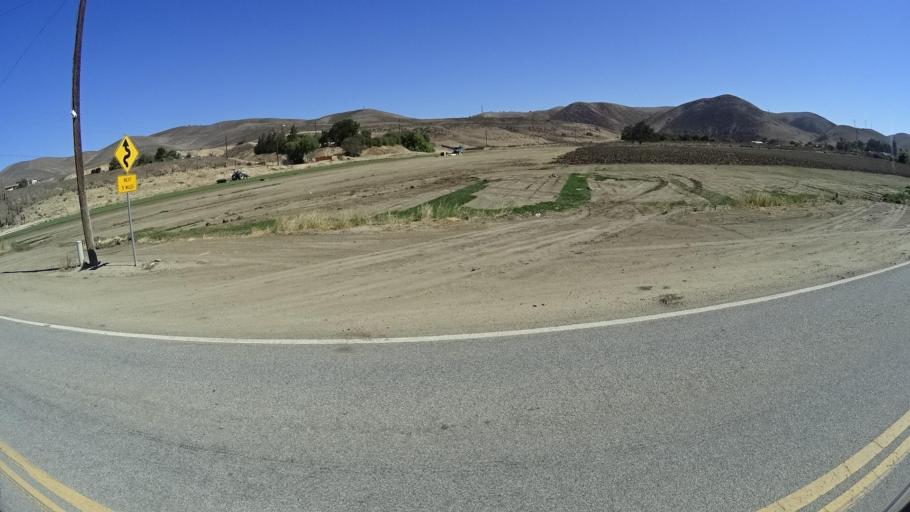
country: US
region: California
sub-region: Monterey County
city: Greenfield
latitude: 36.3564
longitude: -121.2130
